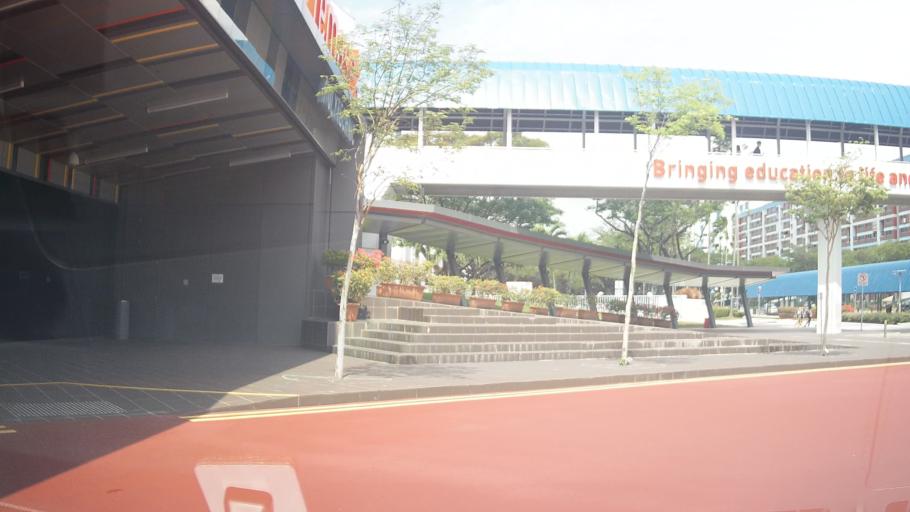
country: SG
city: Singapore
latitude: 1.3462
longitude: 103.9331
